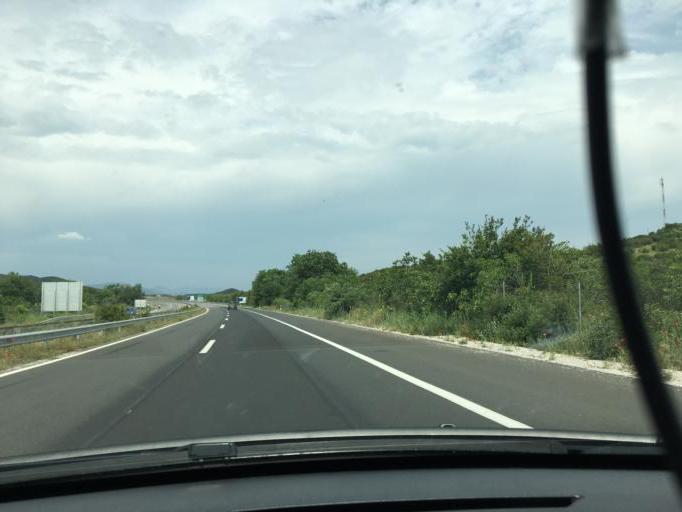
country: MK
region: Gevgelija
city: Miravci
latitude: 41.2520
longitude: 22.4799
